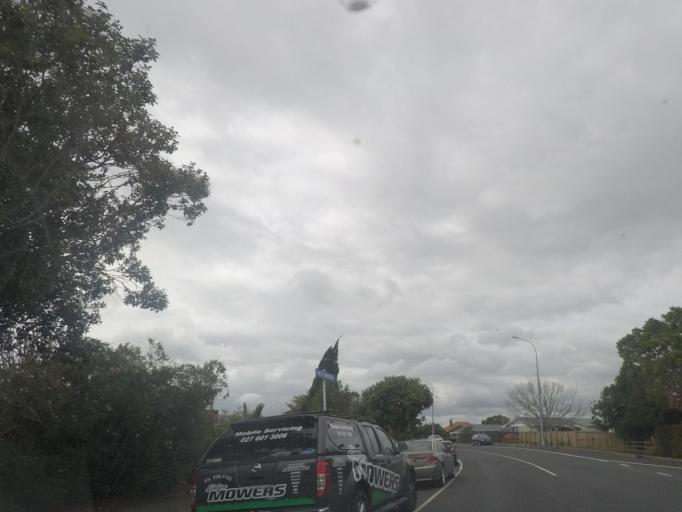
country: NZ
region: Auckland
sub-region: Auckland
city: Tamaki
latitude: -36.8690
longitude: 174.8569
